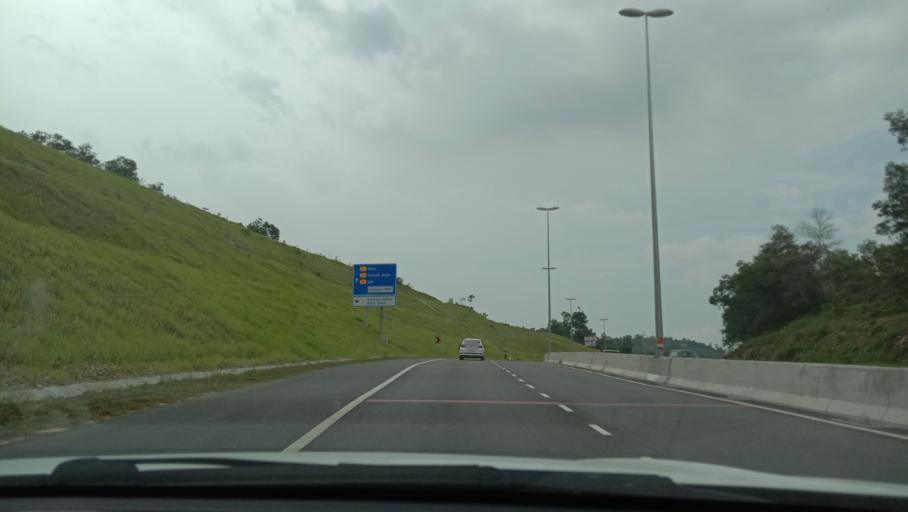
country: MY
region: Selangor
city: Kampung Baru Subang
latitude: 3.1292
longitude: 101.5067
